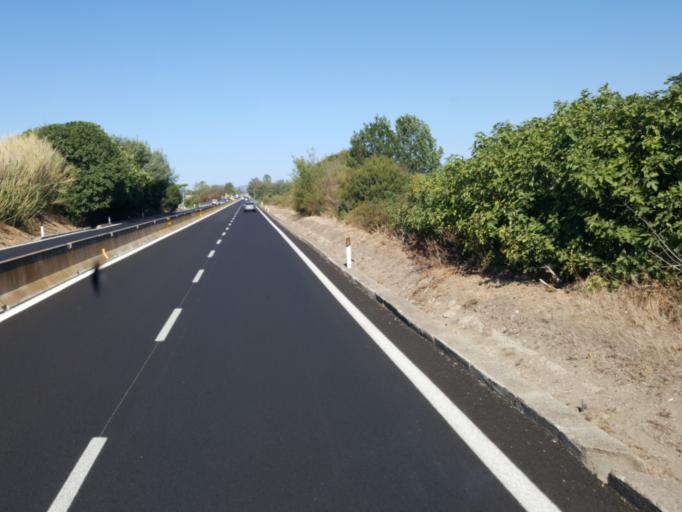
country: IT
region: Latium
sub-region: Provincia di Viterbo
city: Pescia Romana
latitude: 42.3961
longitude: 11.5219
